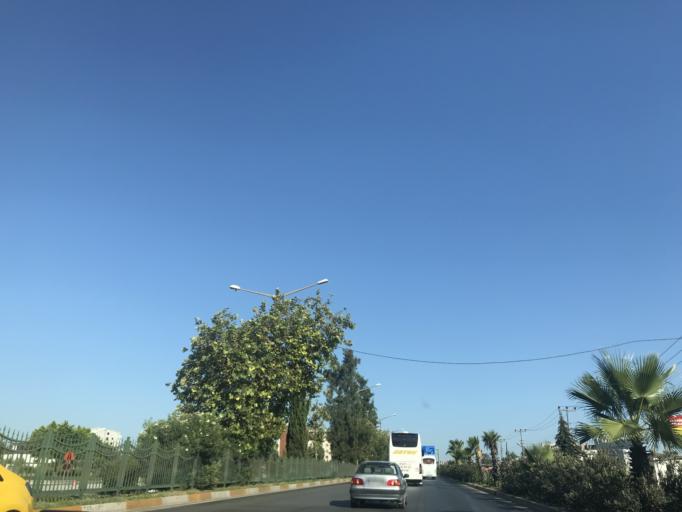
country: TR
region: Antalya
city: Antalya
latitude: 36.9041
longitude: 30.7548
